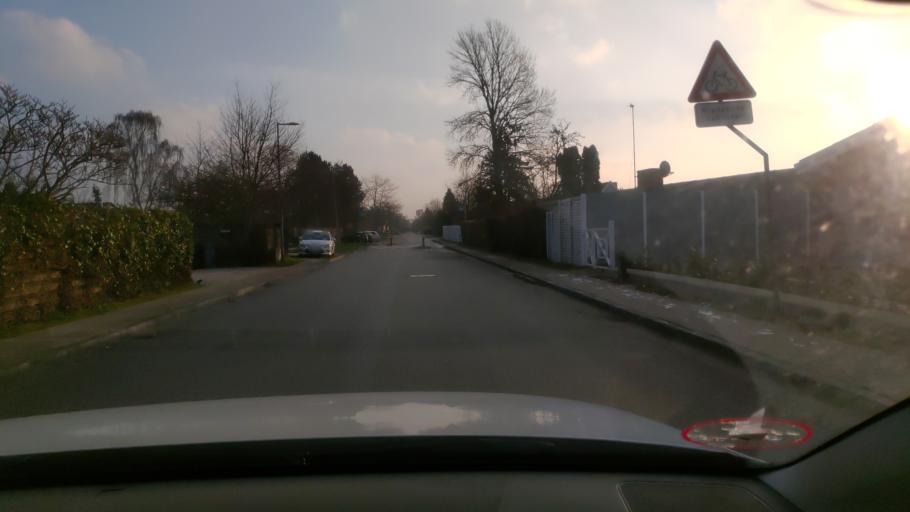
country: DK
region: Zealand
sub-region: Solrod Kommune
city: Solrod Strand
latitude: 55.5384
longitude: 12.2147
